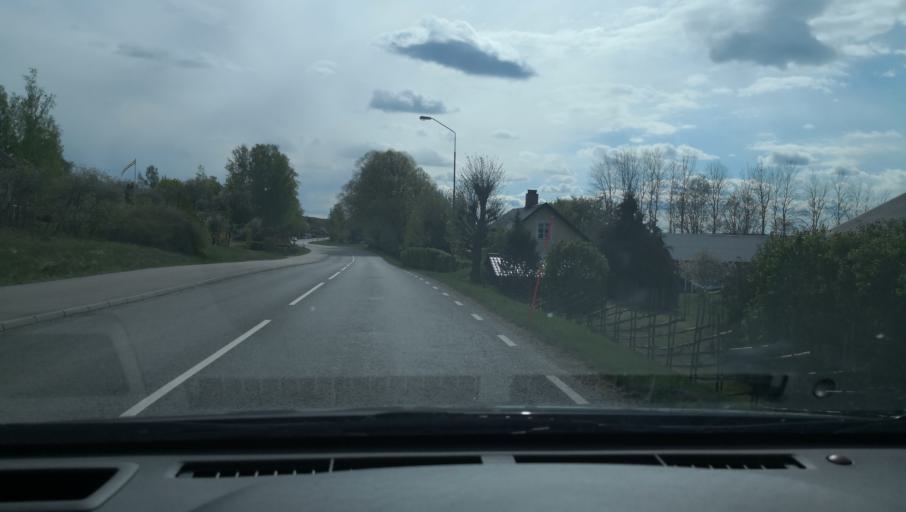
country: SE
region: OErebro
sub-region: Hallsbergs Kommun
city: Hallsberg
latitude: 59.0771
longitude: 15.1453
